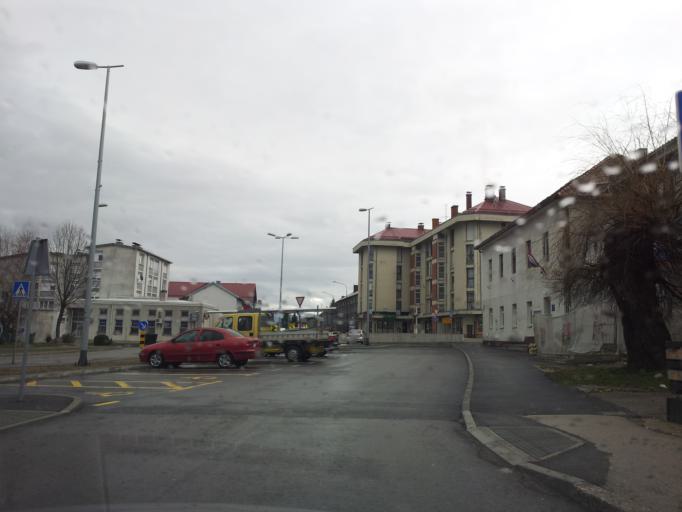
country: BA
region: Federation of Bosnia and Herzegovina
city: Izacic
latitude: 44.7443
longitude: 15.7060
